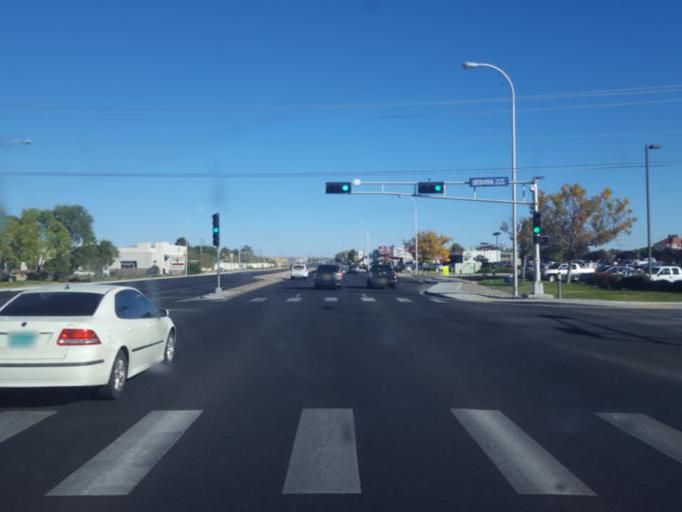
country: US
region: New Mexico
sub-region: Bernalillo County
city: Lee Acres
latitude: 35.1212
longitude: -106.7016
